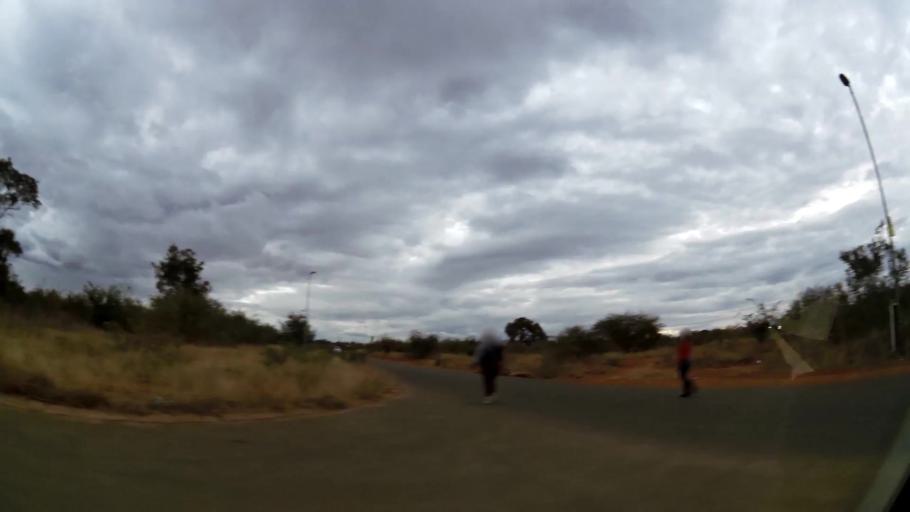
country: ZA
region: Limpopo
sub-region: Waterberg District Municipality
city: Mokopane
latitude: -24.1998
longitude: 28.9978
